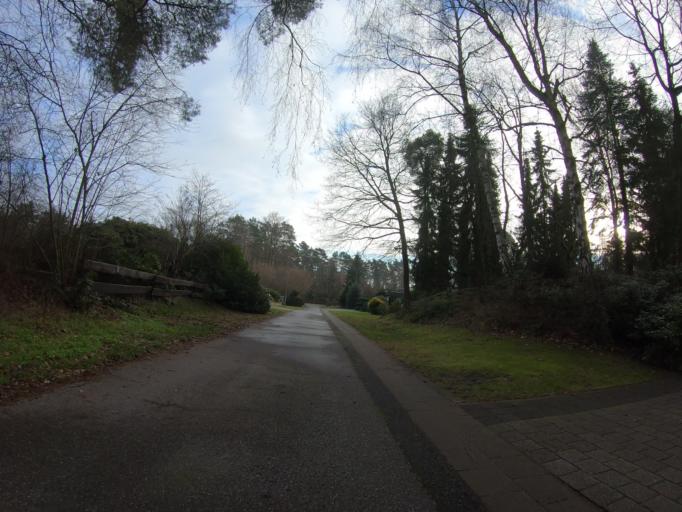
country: DE
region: Lower Saxony
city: Ribbesbuttel
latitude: 52.4862
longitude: 10.4762
